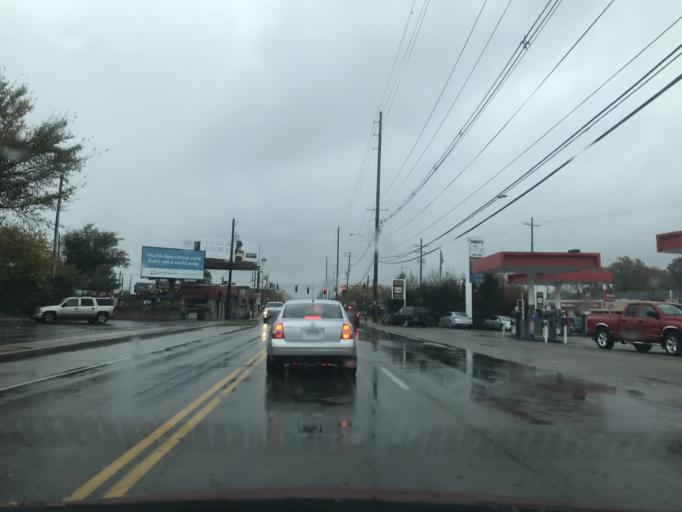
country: US
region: Kentucky
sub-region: Jefferson County
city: Saint Matthews
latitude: 38.2531
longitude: -85.6585
